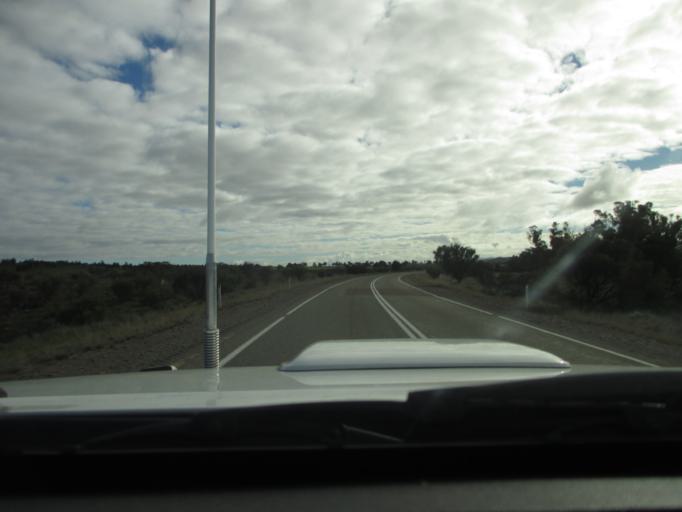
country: AU
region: South Australia
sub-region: Flinders Ranges
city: Quorn
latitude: -32.5088
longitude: 138.5463
